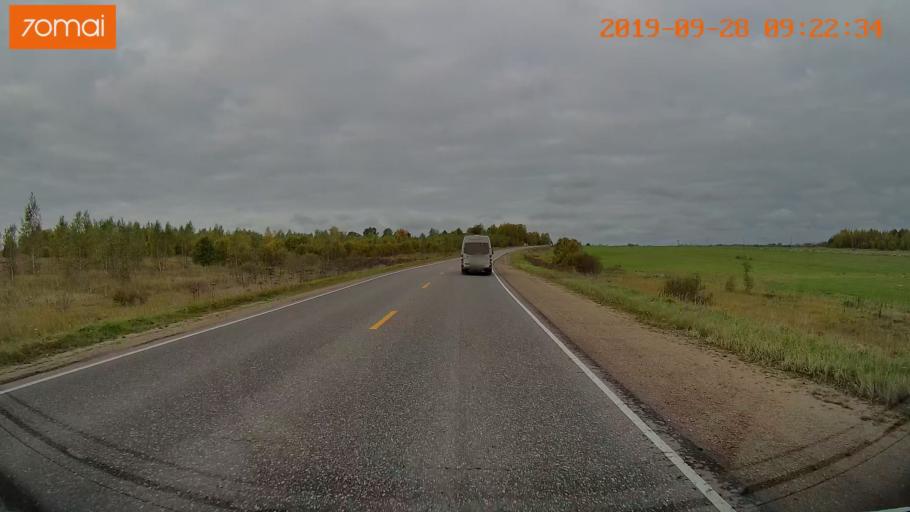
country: RU
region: Ivanovo
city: Pistsovo
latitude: 57.1904
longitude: 40.3768
